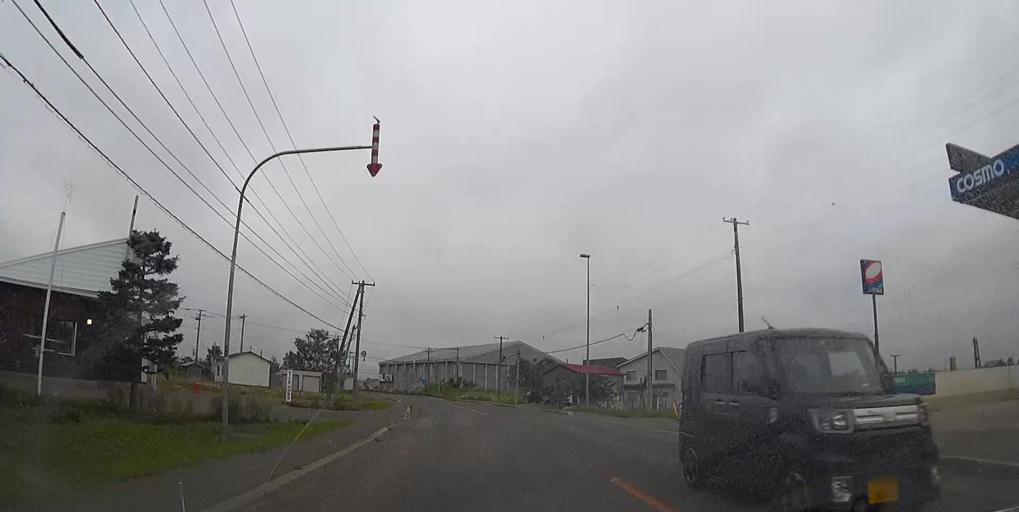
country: JP
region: Hokkaido
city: Iwanai
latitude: 42.4286
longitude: 140.0022
